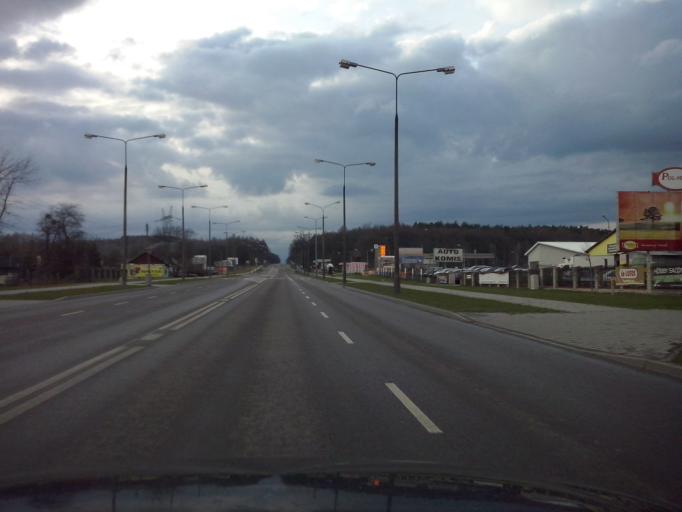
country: PL
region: Lublin Voivodeship
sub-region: Chelm
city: Chelm
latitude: 51.1479
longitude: 23.4319
